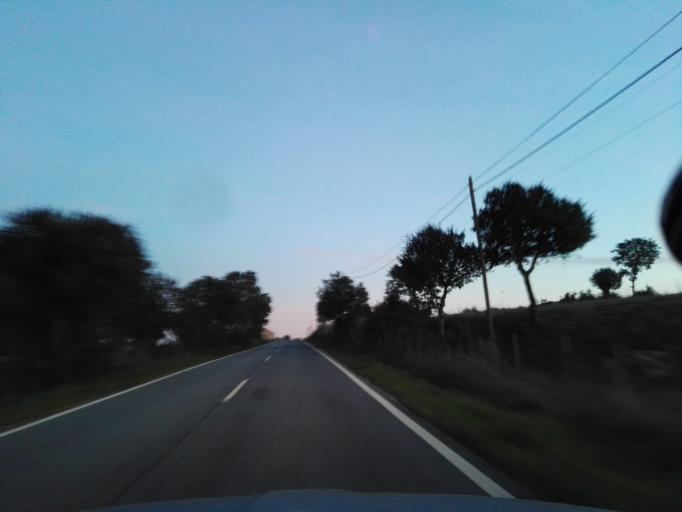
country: PT
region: Evora
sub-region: Arraiolos
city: Arraiolos
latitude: 38.7200
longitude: -8.0526
